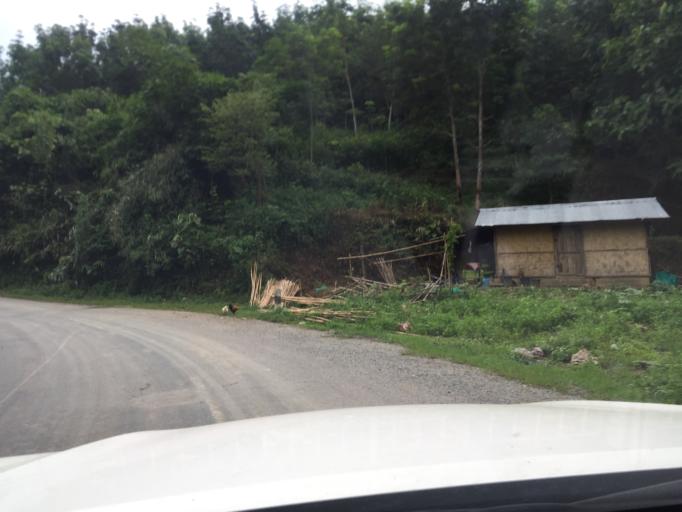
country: LA
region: Oudomxai
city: Muang La
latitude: 21.1088
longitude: 102.2018
